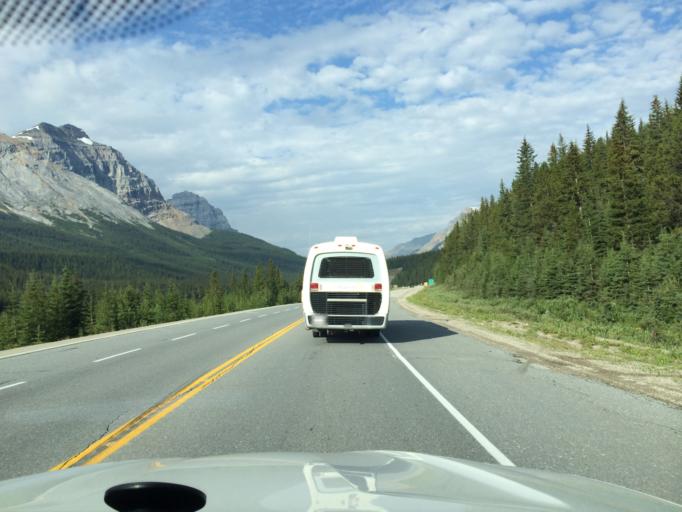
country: CA
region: Alberta
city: Lake Louise
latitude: 51.4430
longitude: -116.3393
